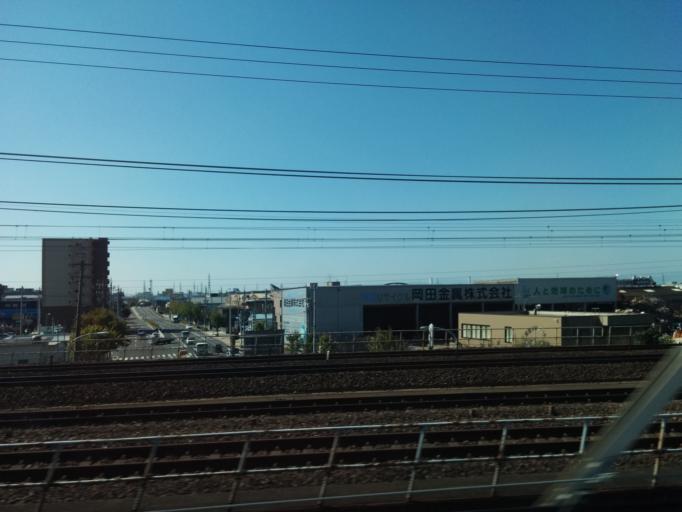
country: JP
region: Aichi
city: Obu
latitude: 35.0726
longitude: 136.9387
